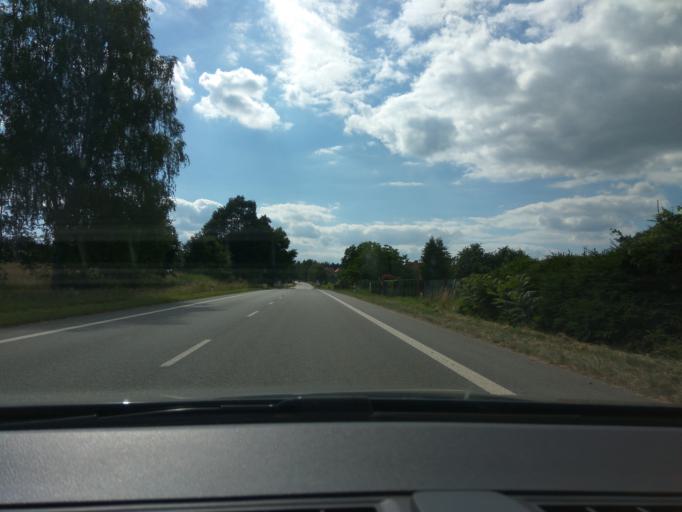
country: CZ
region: Jihocesky
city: Cimelice
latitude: 49.5031
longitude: 14.1692
